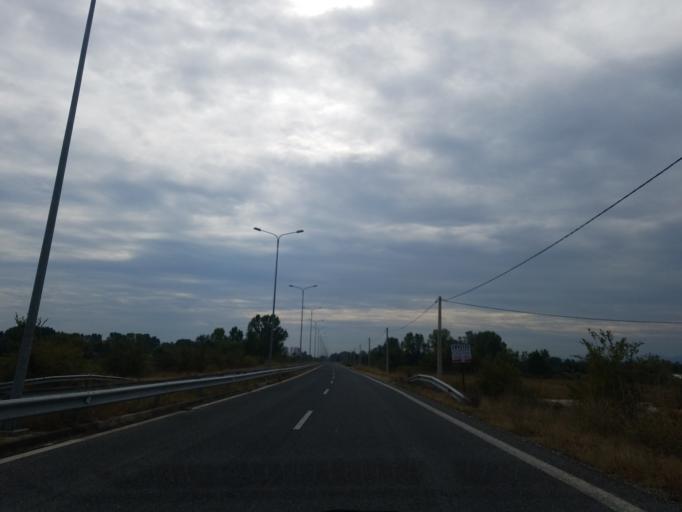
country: GR
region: Thessaly
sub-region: Trikala
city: Pyrgetos
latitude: 39.5360
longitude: 21.7376
